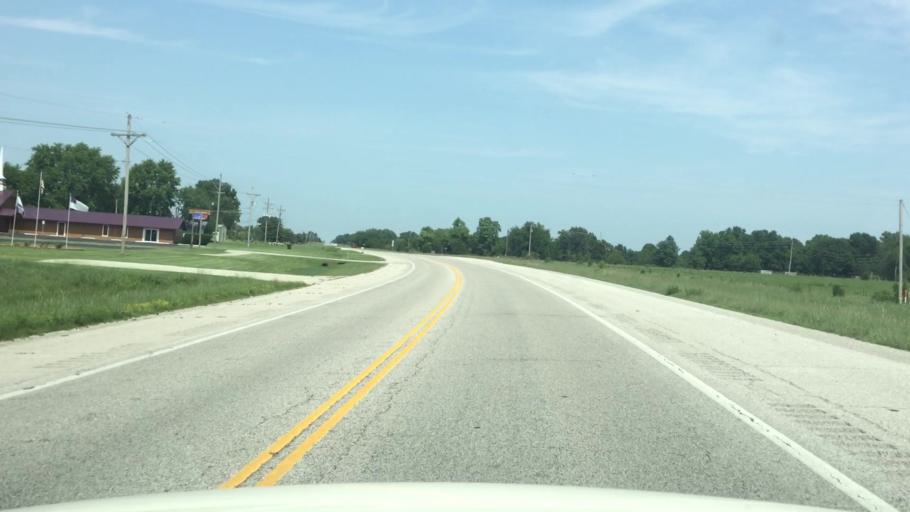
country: US
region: Kansas
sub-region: Cherokee County
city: Galena
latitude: 37.0872
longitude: -94.7045
